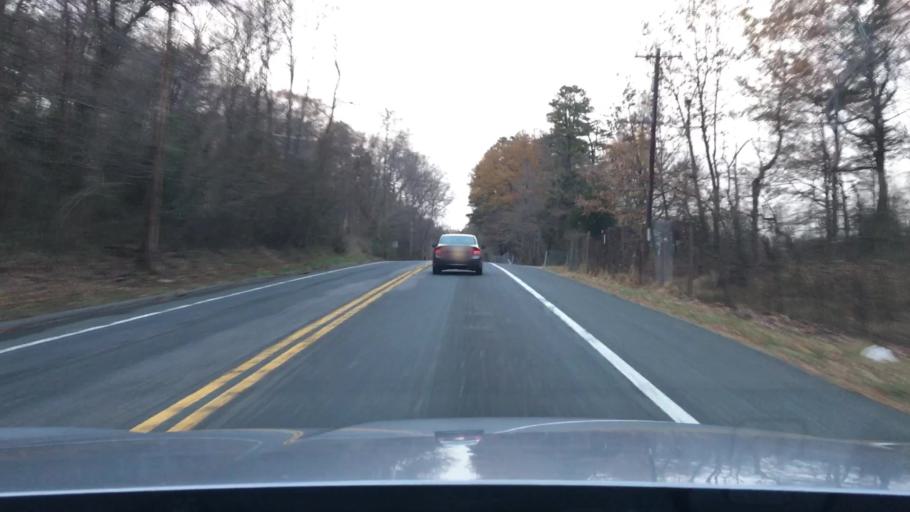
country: US
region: Maryland
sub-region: Prince George's County
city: Glenn Dale
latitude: 39.0346
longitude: -76.7902
